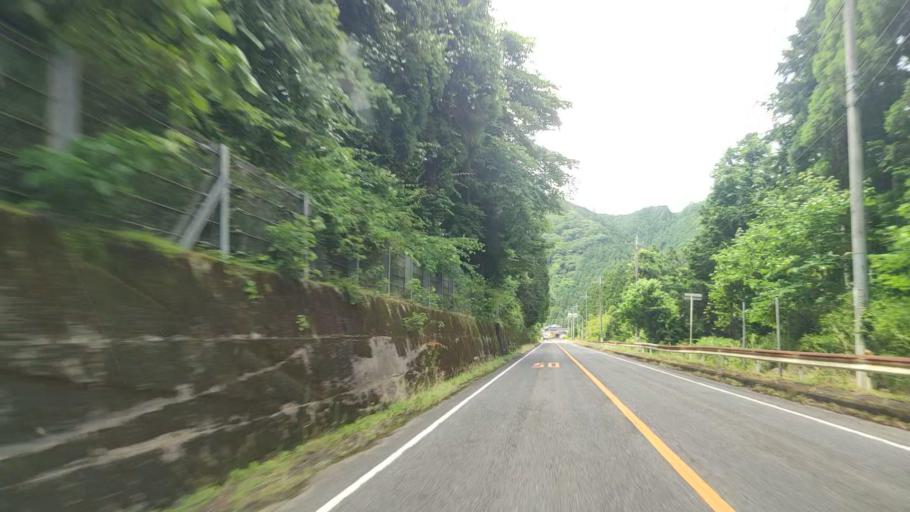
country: JP
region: Okayama
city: Niimi
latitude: 35.0872
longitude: 133.6480
